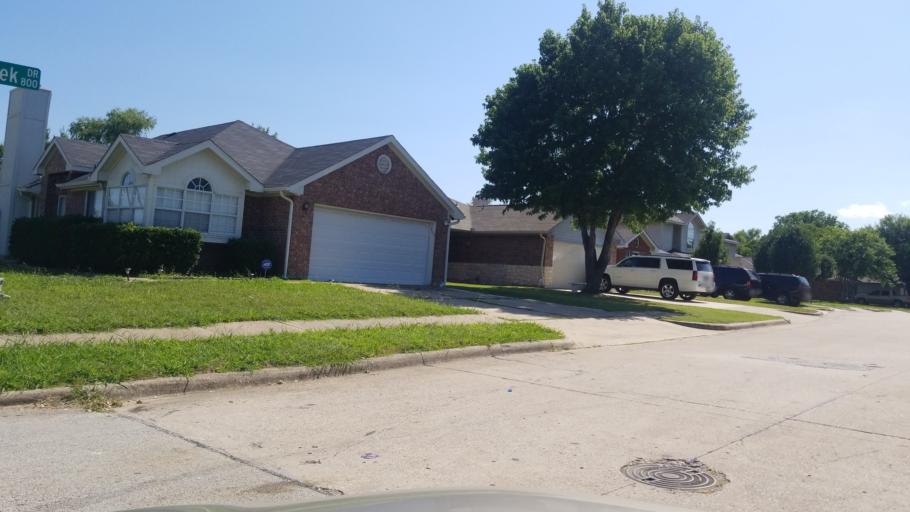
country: US
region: Texas
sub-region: Dallas County
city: Grand Prairie
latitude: 32.6932
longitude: -97.0158
